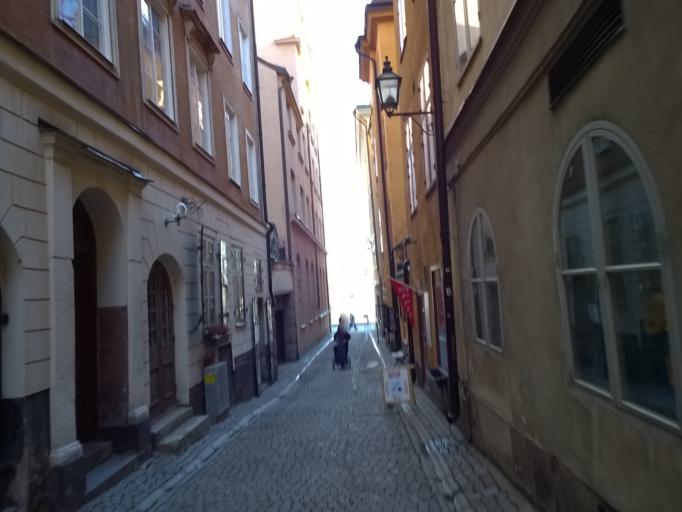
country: SE
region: Stockholm
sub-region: Stockholms Kommun
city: Stockholm
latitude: 59.3256
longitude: 18.0741
